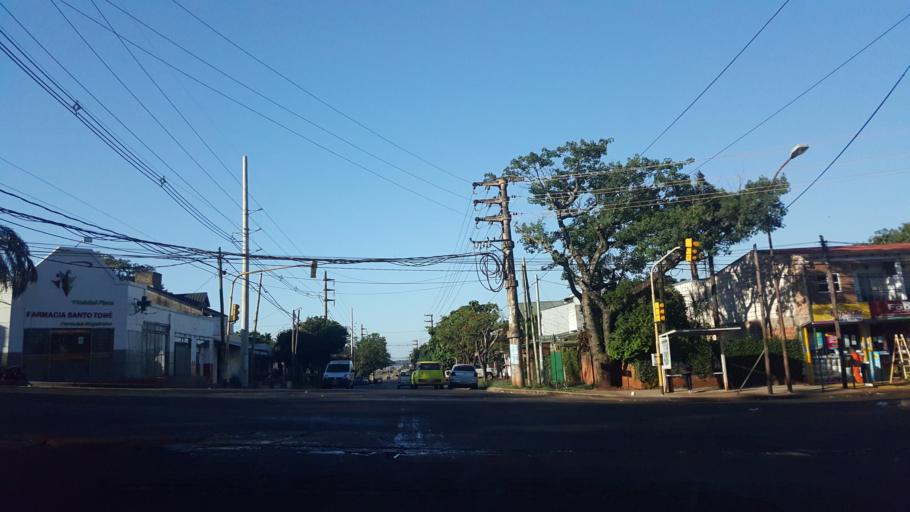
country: AR
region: Misiones
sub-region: Departamento de Capital
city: Posadas
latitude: -27.3604
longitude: -55.9042
